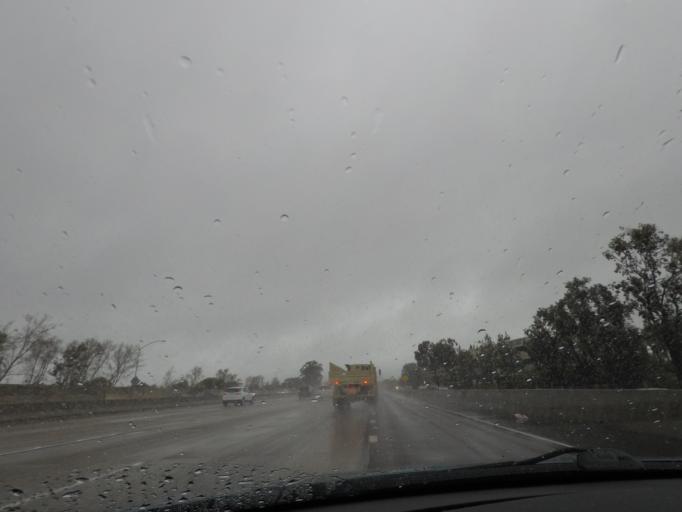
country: US
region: California
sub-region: San Diego County
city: San Diego
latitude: 32.7949
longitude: -117.1573
